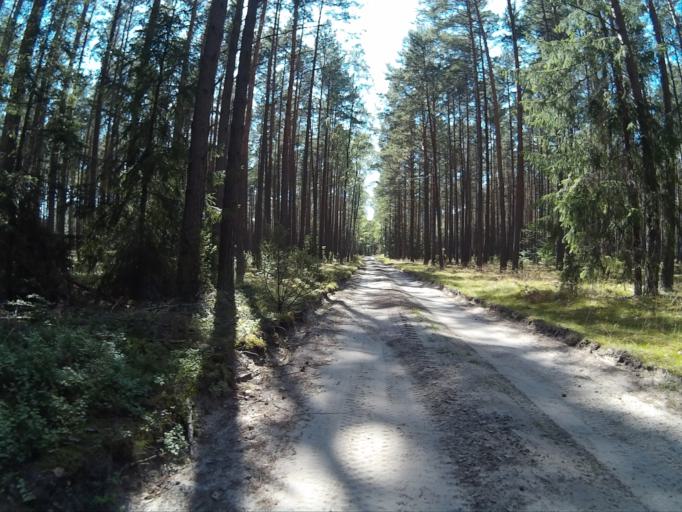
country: PL
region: Pomeranian Voivodeship
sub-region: Powiat chojnicki
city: Czersk
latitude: 53.7210
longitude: 17.8872
